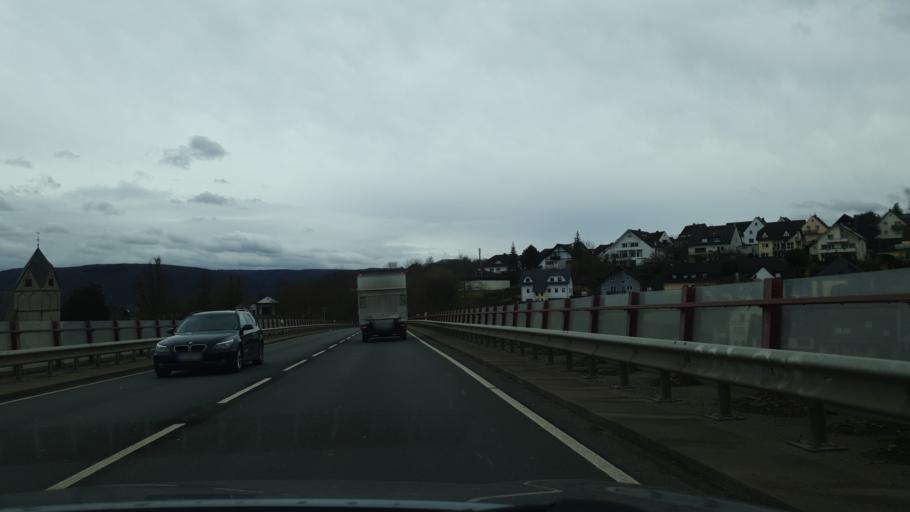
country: DE
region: Rheinland-Pfalz
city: Rhens
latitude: 50.2810
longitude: 7.6153
